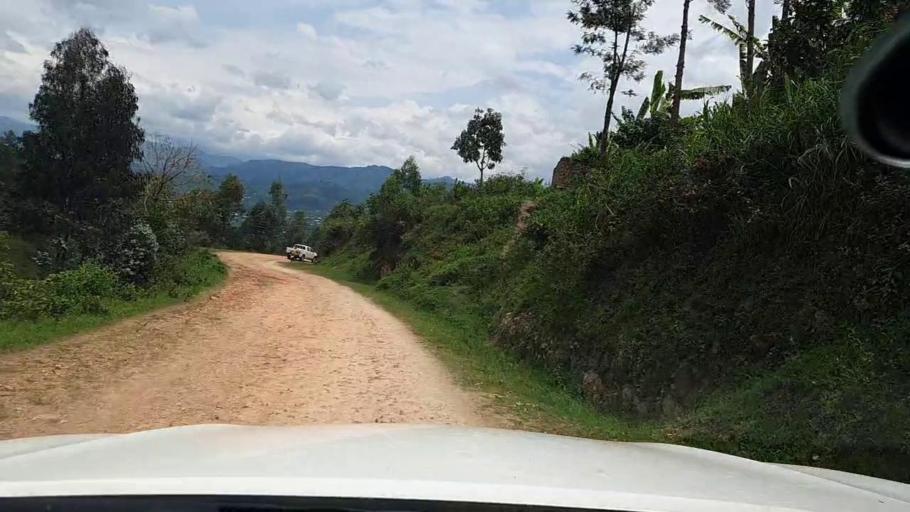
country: RW
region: Western Province
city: Kibuye
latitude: -2.0850
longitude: 29.4157
